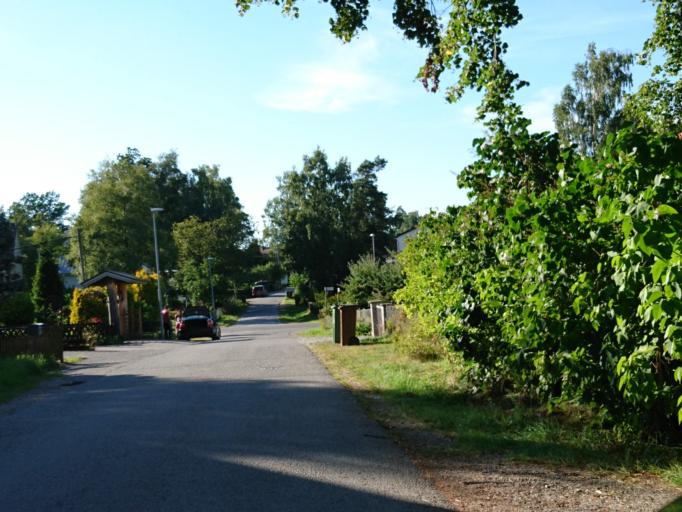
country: SE
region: Stockholm
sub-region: Huddinge Kommun
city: Segeltorp
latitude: 59.2657
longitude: 17.9545
